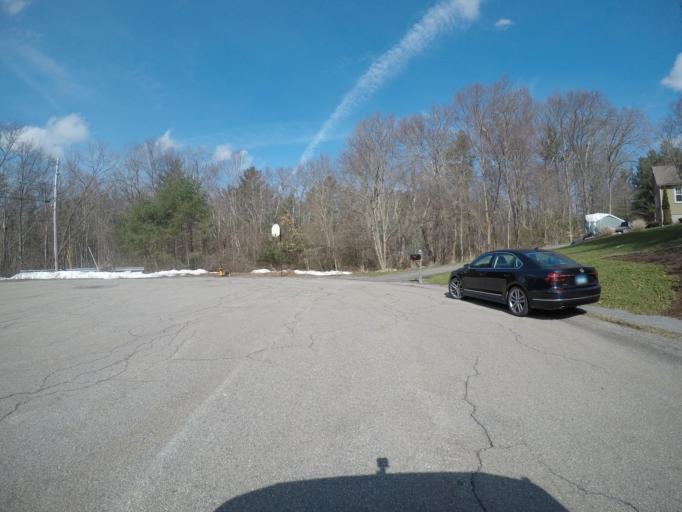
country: US
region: Massachusetts
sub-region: Bristol County
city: Easton
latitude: 42.0194
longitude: -71.1452
